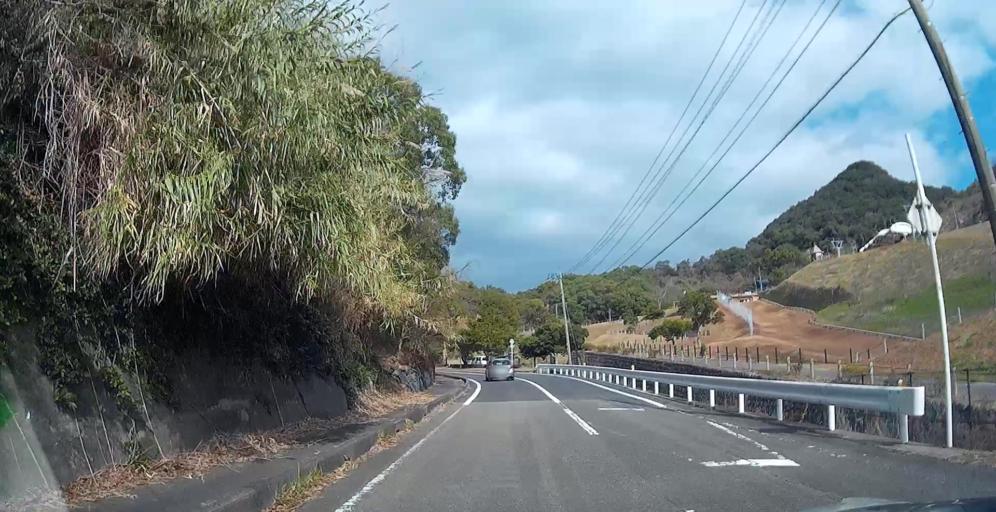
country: JP
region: Kumamoto
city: Minamata
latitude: 32.3213
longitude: 130.4712
